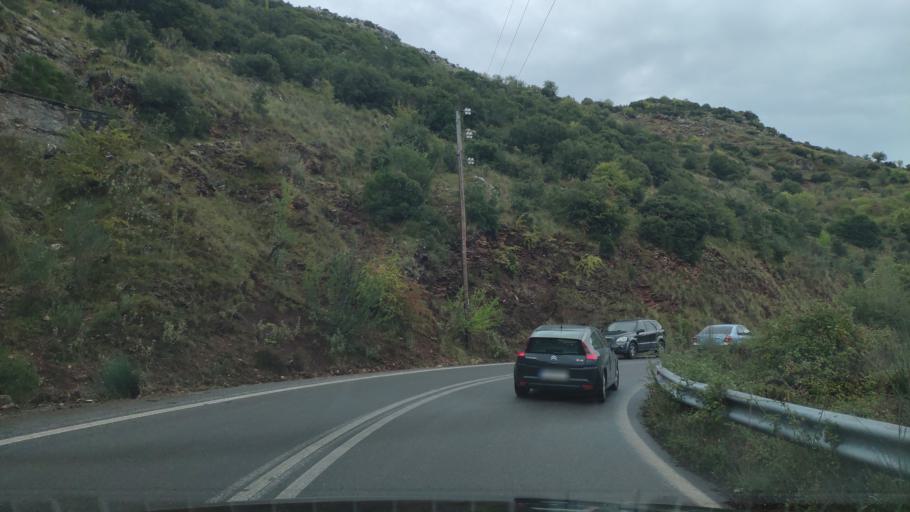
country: GR
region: Peloponnese
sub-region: Nomos Arkadias
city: Dimitsana
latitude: 37.6072
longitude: 22.0424
